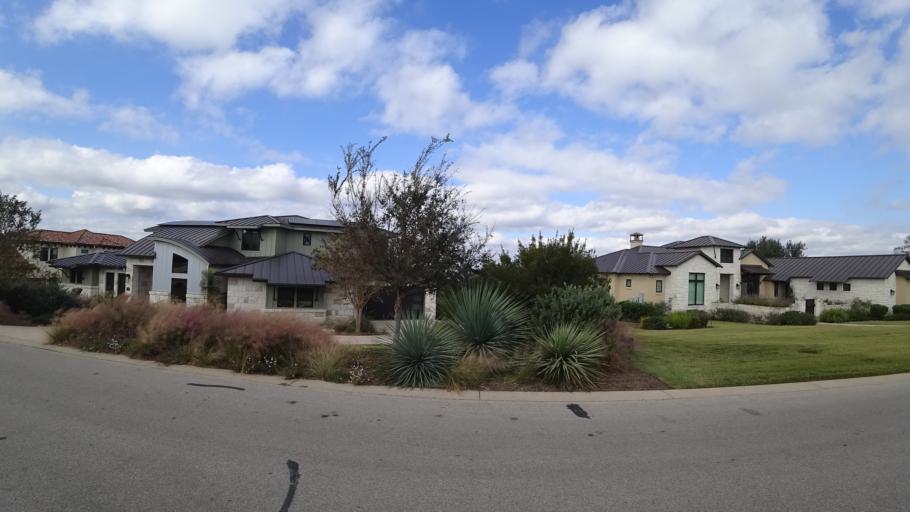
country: US
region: Texas
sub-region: Travis County
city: Bee Cave
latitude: 30.2490
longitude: -97.9272
